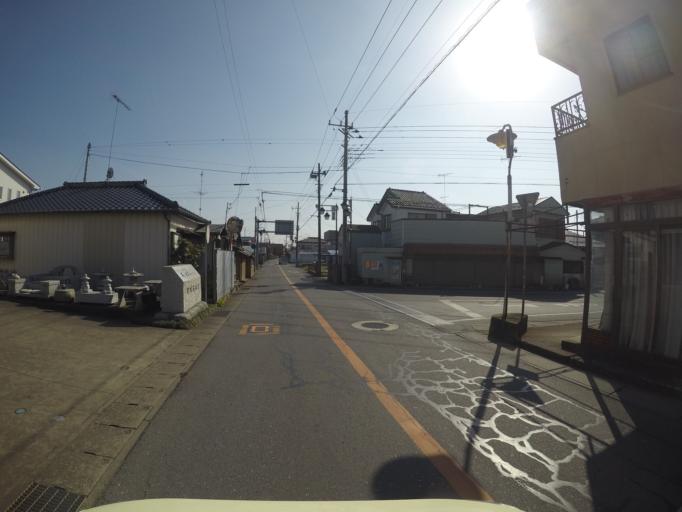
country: JP
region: Ibaraki
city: Yuki
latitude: 36.3083
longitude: 139.8760
